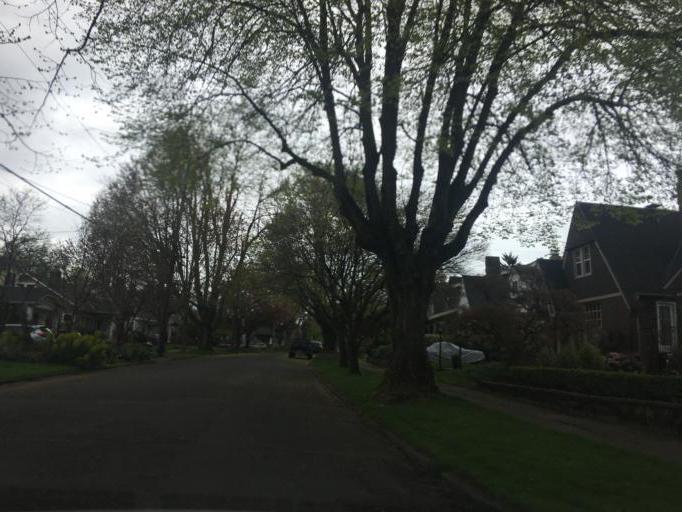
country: US
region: Oregon
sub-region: Multnomah County
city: Portland
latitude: 45.5295
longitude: -122.6256
